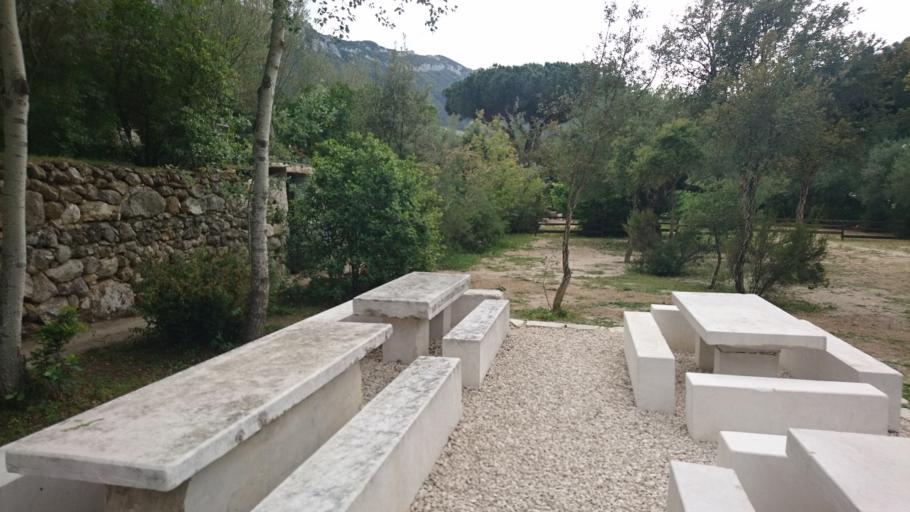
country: IT
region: Sardinia
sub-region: Provincia di Nuoro
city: Cala Gonone
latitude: 40.3072
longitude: 9.6291
